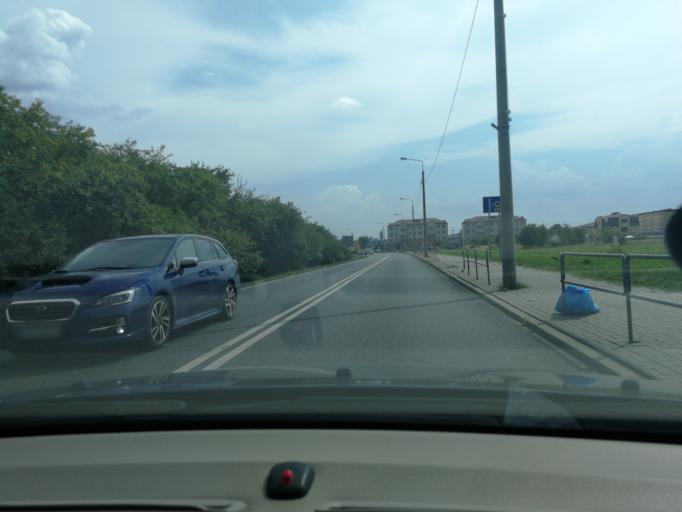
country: PL
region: Masovian Voivodeship
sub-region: Powiat zyrardowski
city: Mszczonow
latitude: 51.9793
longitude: 20.5287
